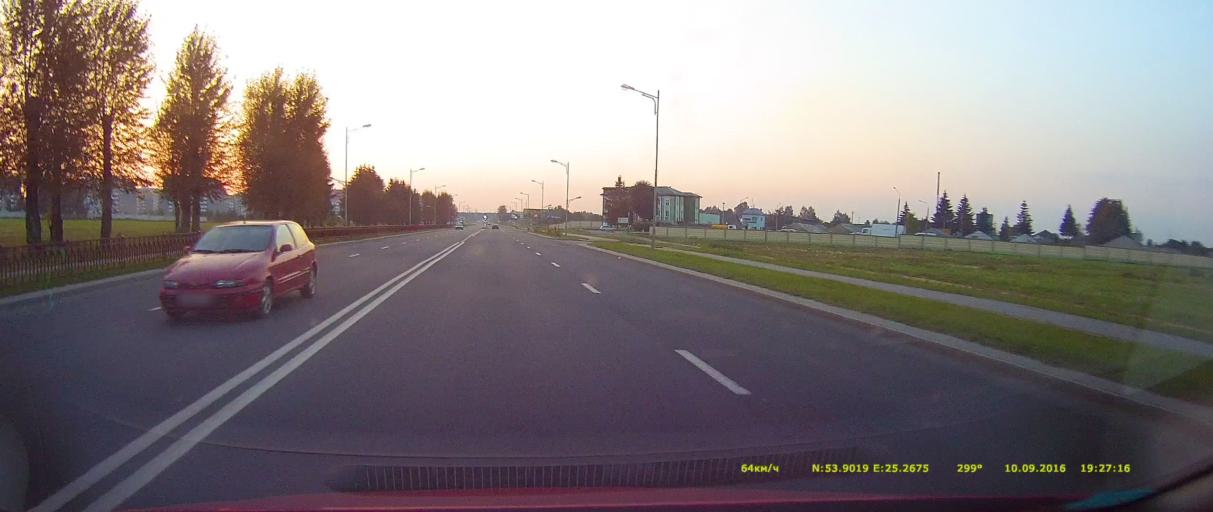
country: BY
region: Grodnenskaya
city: Lida
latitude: 53.9020
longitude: 25.2676
